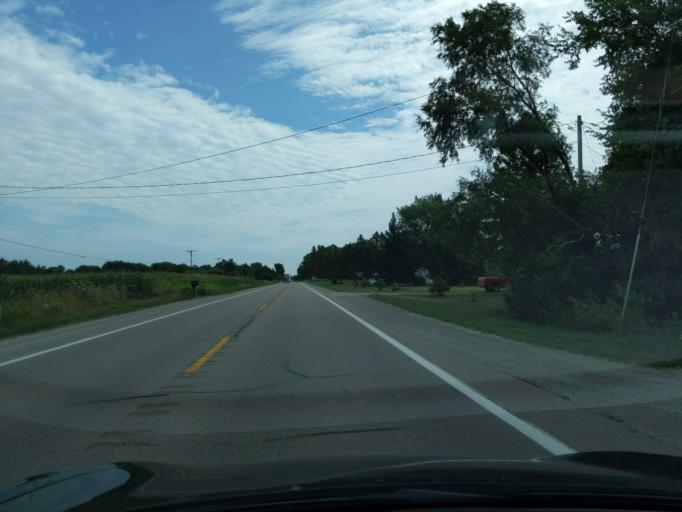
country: US
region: Michigan
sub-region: Gratiot County
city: Breckenridge
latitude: 43.4080
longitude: -84.3968
